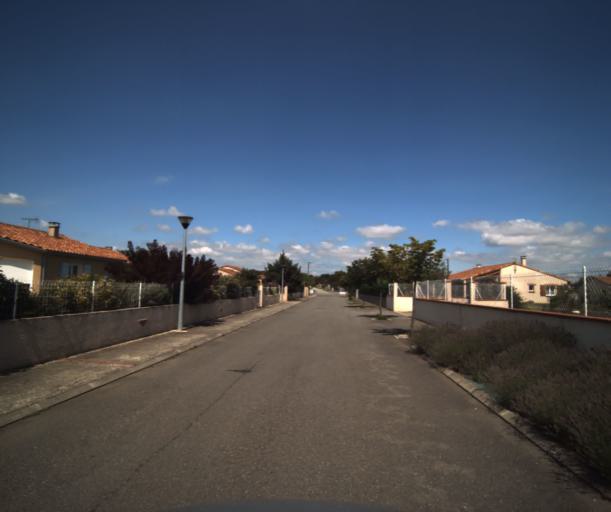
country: FR
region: Midi-Pyrenees
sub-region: Departement de la Haute-Garonne
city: Lacasse
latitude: 43.3925
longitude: 1.2589
